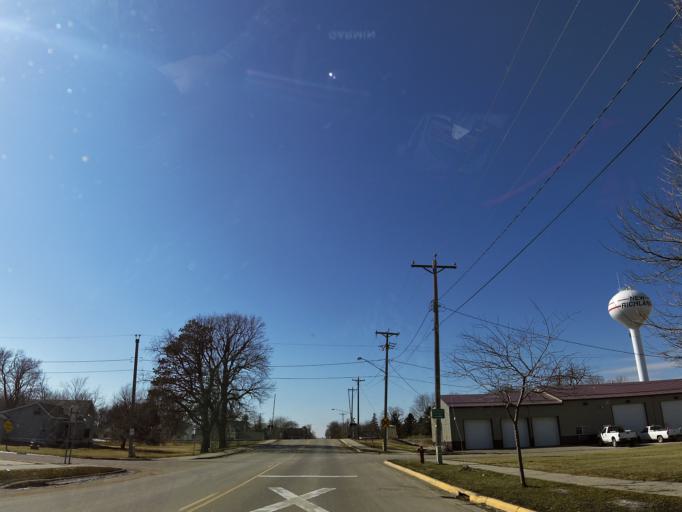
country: US
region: Minnesota
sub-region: Waseca County
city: New Richland
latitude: 43.8918
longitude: -93.4912
